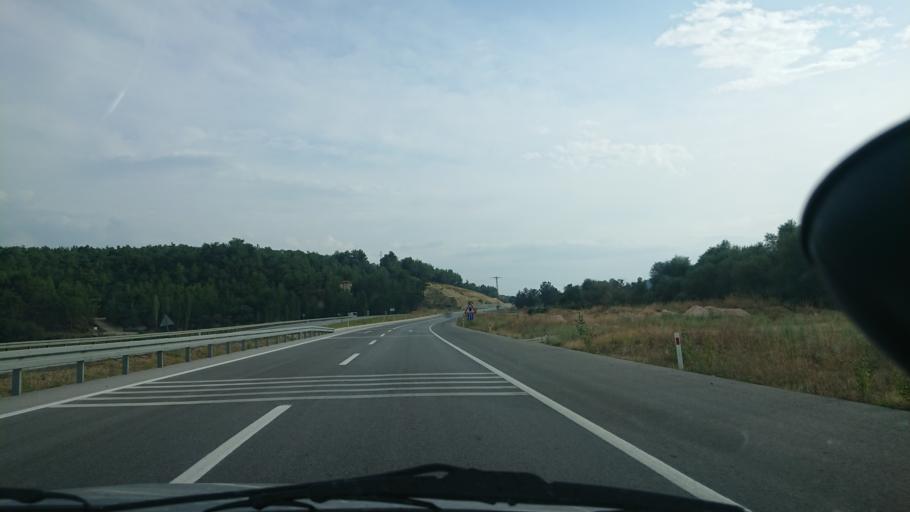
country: TR
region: Kuetahya
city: Gediz
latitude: 38.9279
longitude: 29.3049
